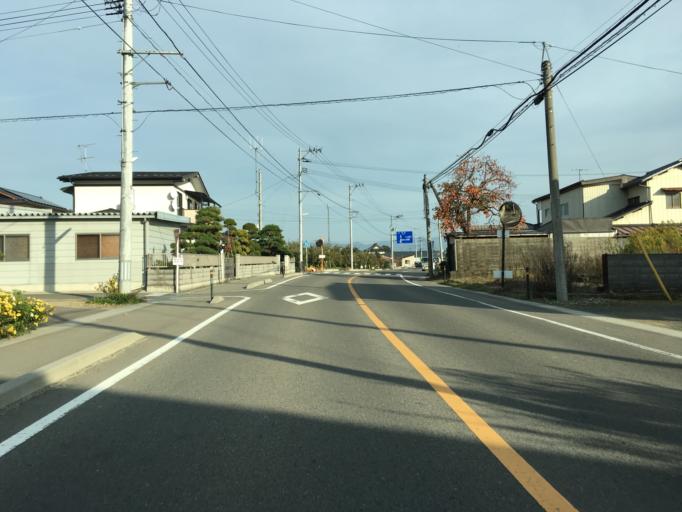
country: JP
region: Fukushima
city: Hobaramachi
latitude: 37.8250
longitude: 140.4756
